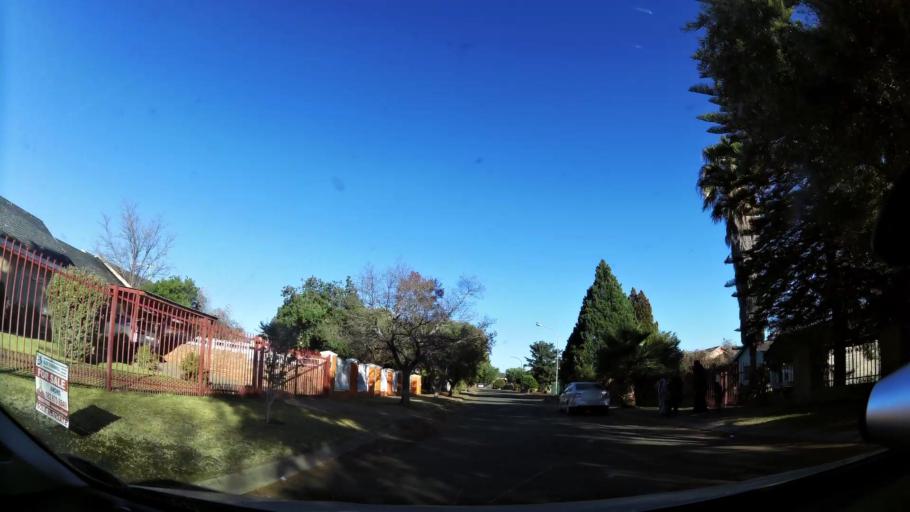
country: ZA
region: Northern Cape
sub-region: Frances Baard District Municipality
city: Kimberley
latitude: -28.7391
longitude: 24.7269
